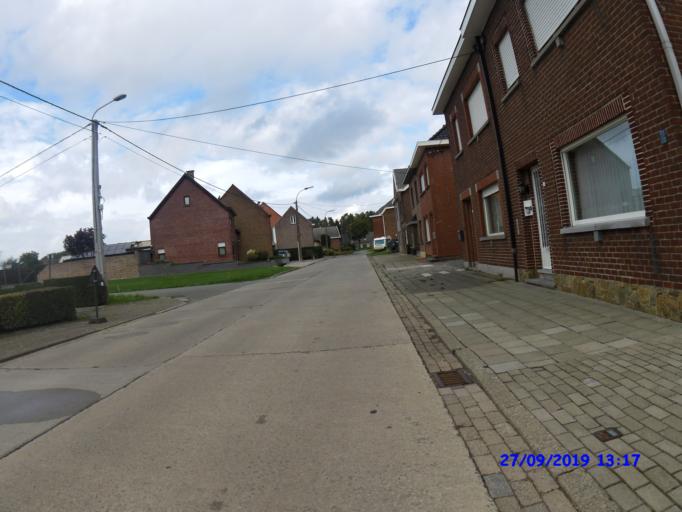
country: BE
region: Flanders
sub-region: Provincie Oost-Vlaanderen
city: Lede
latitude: 50.9467
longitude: 3.9464
